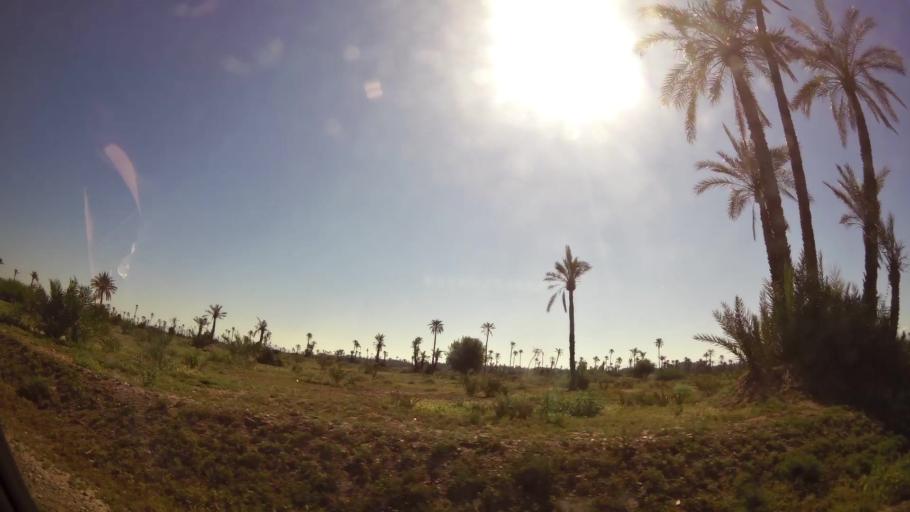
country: MA
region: Marrakech-Tensift-Al Haouz
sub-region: Marrakech
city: Marrakesh
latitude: 31.6629
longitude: -7.9534
